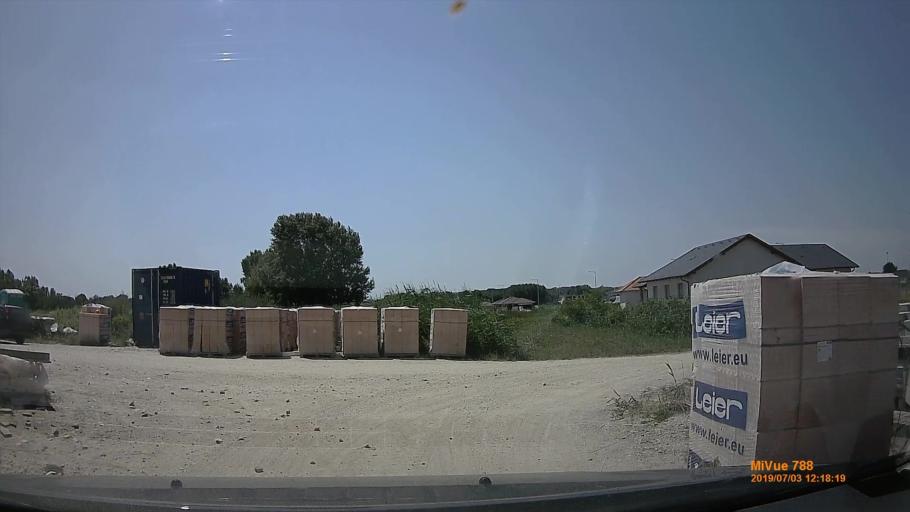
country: HU
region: Gyor-Moson-Sopron
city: Gyor
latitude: 47.7164
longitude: 17.6104
